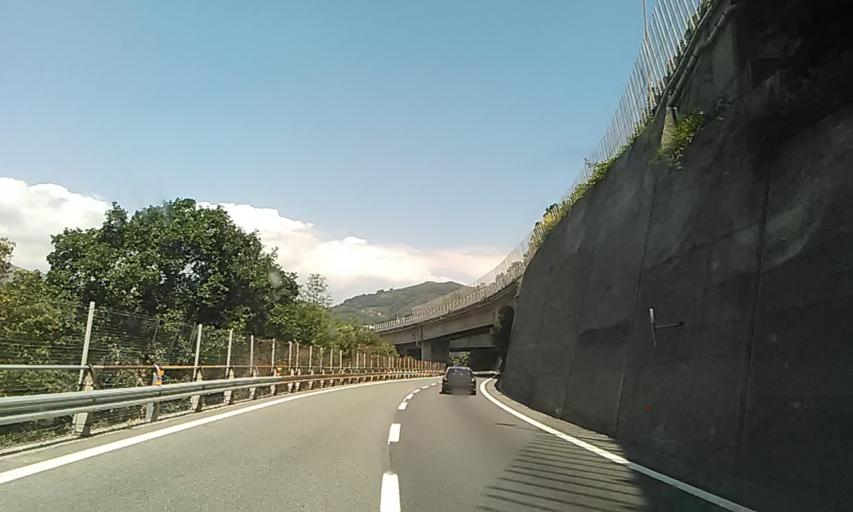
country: IT
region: Liguria
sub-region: Provincia di Genova
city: Mele
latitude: 44.4324
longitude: 8.7409
